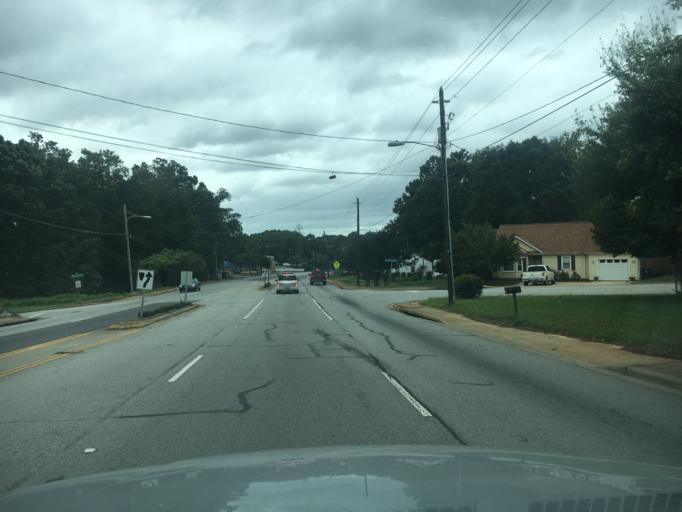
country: US
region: South Carolina
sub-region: Greenville County
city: Greenville
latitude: 34.8860
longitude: -82.3752
